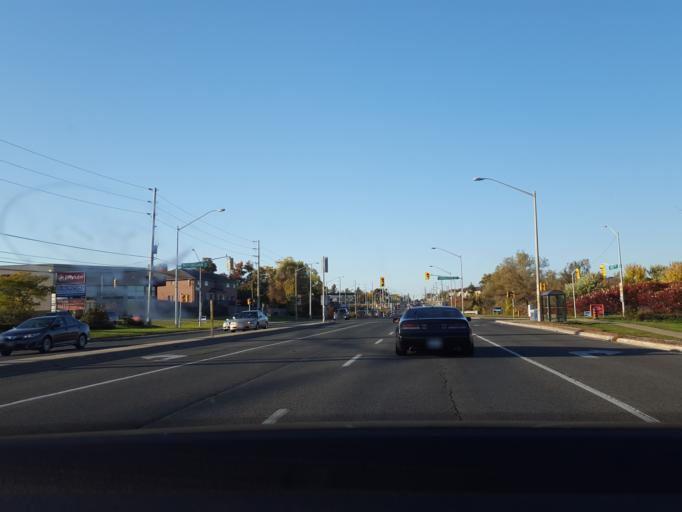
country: CA
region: Ontario
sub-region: York
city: Richmond Hill
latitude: 43.9041
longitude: -79.4448
